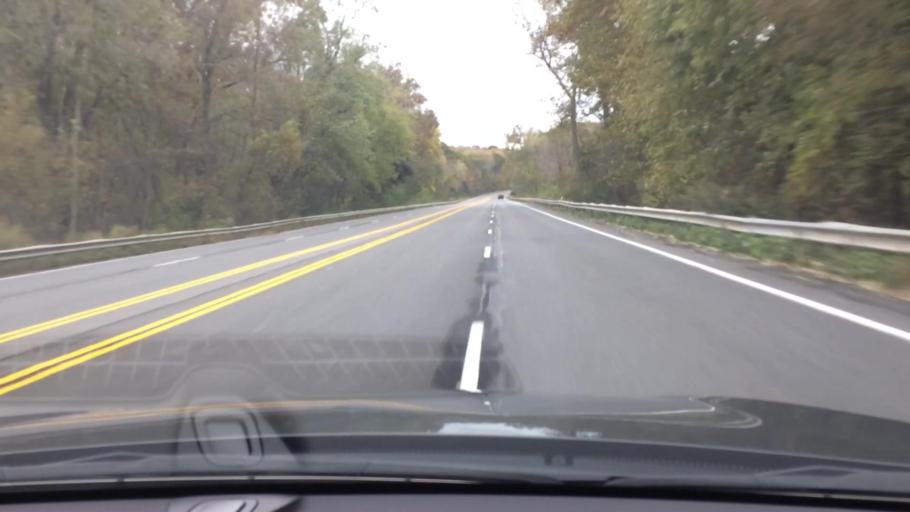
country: US
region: New York
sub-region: Columbia County
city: Kinderhook
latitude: 42.4026
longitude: -73.6886
